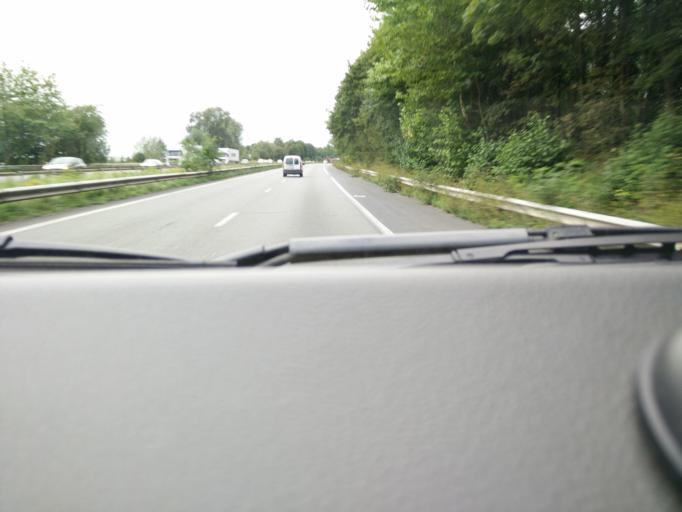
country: FR
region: Nord-Pas-de-Calais
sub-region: Departement du Nord
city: Orchies
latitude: 50.4679
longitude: 3.2358
